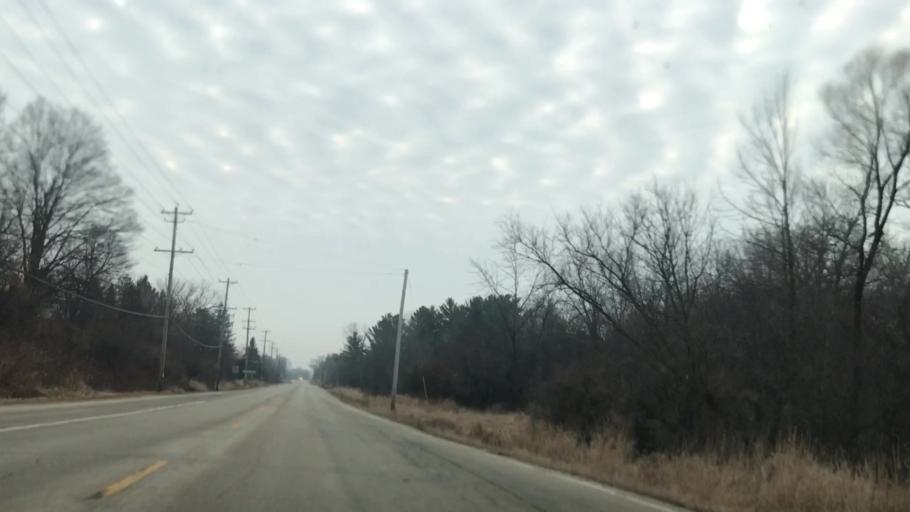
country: US
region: Wisconsin
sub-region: Ozaukee County
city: Cedarburg
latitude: 43.2874
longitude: -88.0041
